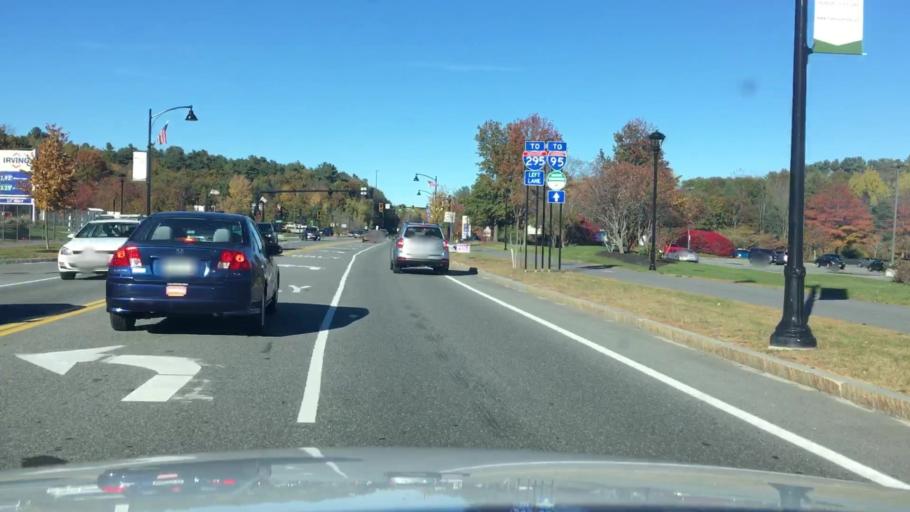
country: US
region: Maine
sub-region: Cumberland County
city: Falmouth
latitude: 43.7247
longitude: -70.2320
